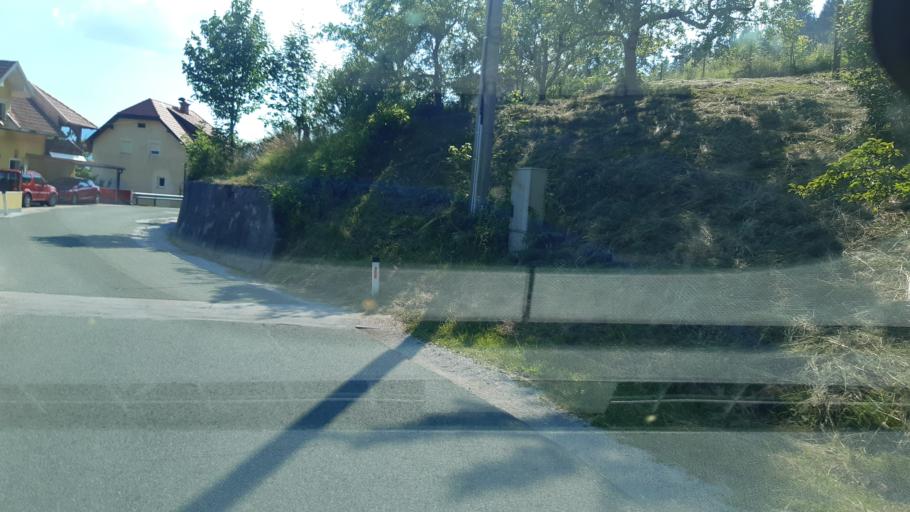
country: SI
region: Trzic
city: Bistrica pri Trzicu
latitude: 46.3608
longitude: 14.2627
